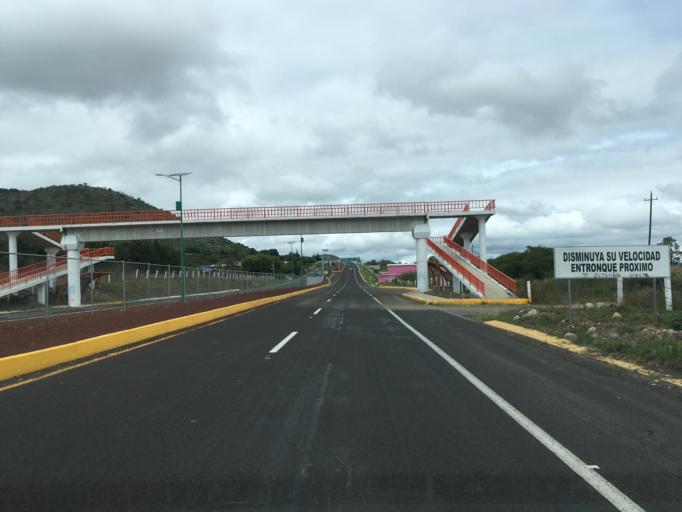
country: MX
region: Hidalgo
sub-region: Atotonilco el Grande
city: La Estancia
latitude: 20.3295
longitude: -98.7002
